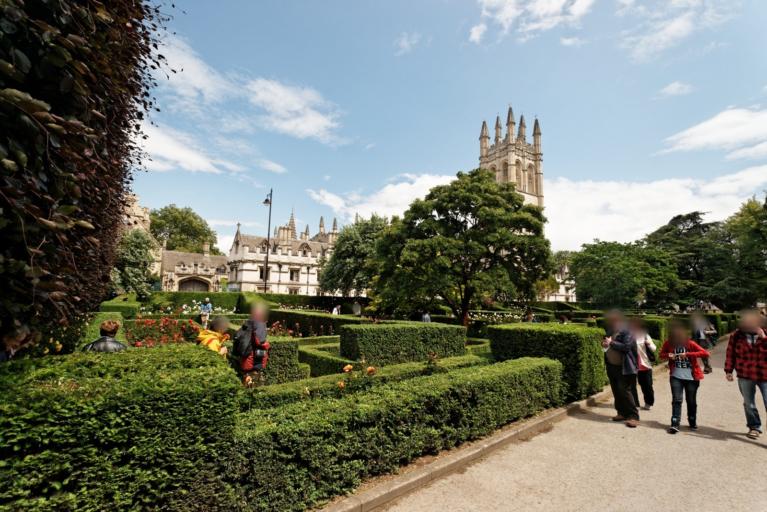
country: GB
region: England
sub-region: Oxfordshire
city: Oxford
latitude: 51.7517
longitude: -1.2480
